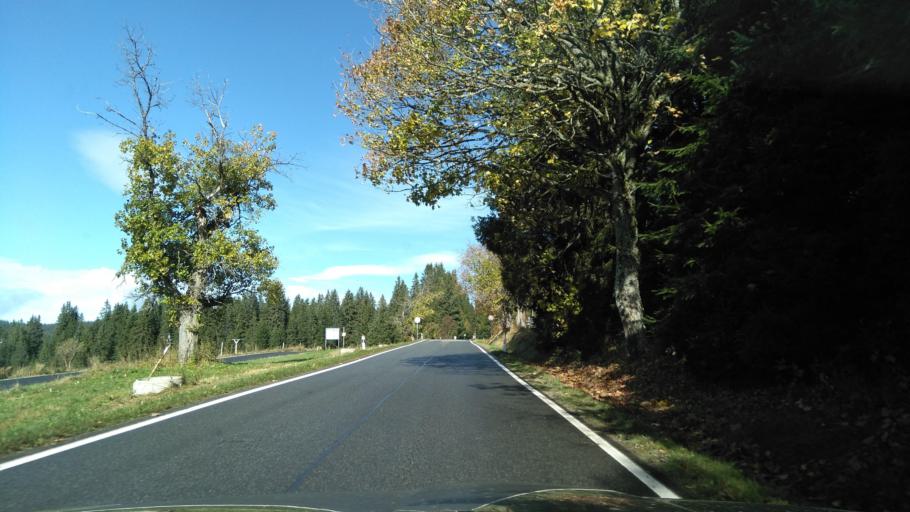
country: CZ
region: Jihocesky
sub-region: Okres Prachatice
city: Borova Lada
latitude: 49.0291
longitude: 13.5788
